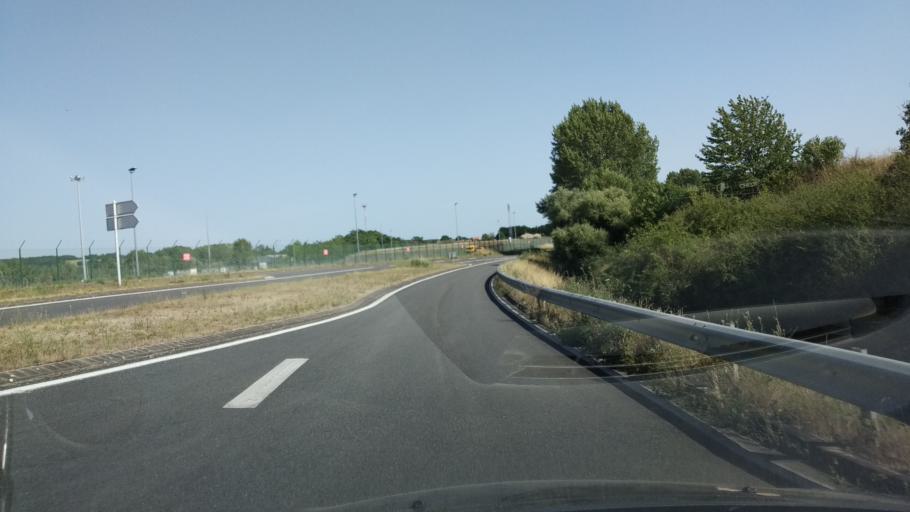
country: FR
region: Poitou-Charentes
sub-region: Departement de la Vienne
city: Lussac-les-Chateaux
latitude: 46.4474
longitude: 0.6536
